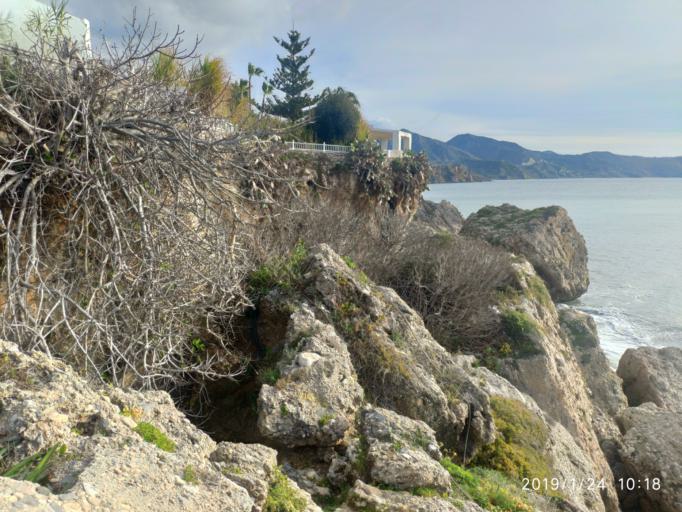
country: ES
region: Andalusia
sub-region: Provincia de Malaga
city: Nerja
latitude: 36.7455
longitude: -3.8746
